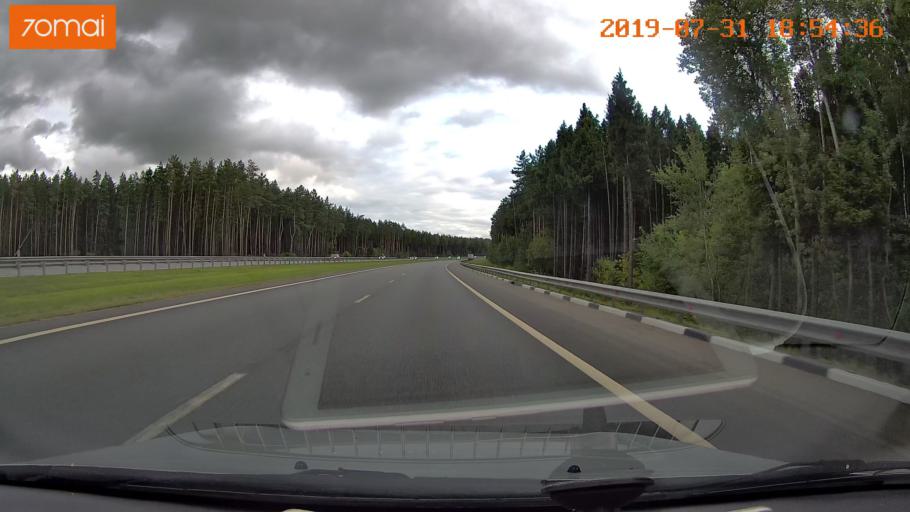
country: RU
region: Moskovskaya
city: Raduzhnyy
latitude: 55.1873
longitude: 38.6689
